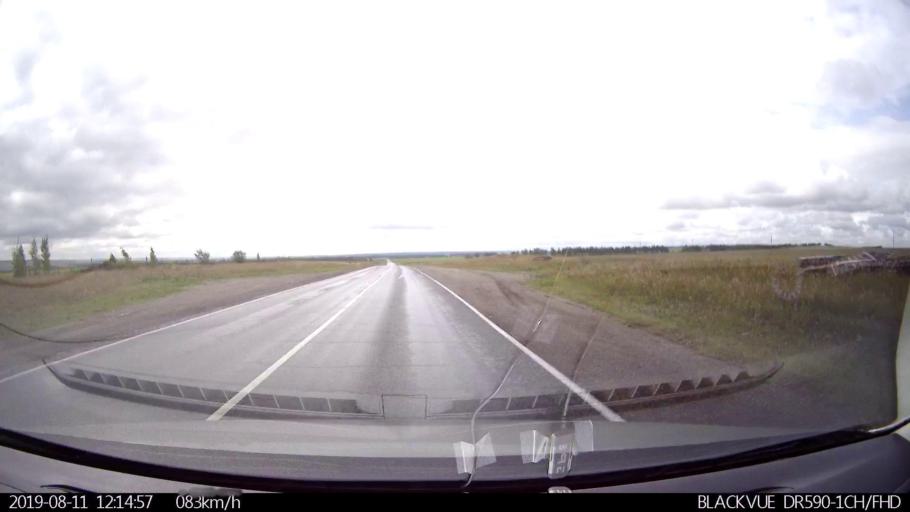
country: RU
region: Ulyanovsk
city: Ignatovka
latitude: 53.9469
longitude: 47.9733
